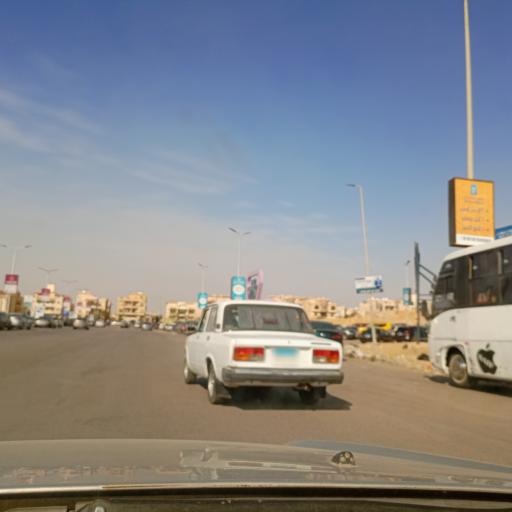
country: EG
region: Muhafazat al Qahirah
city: Cairo
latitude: 30.0195
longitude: 31.4328
